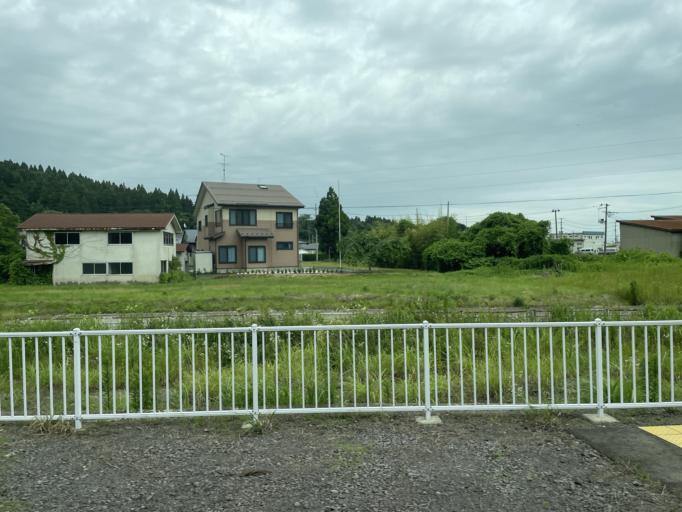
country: JP
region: Akita
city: Tenno
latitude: 39.9044
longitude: 139.8618
